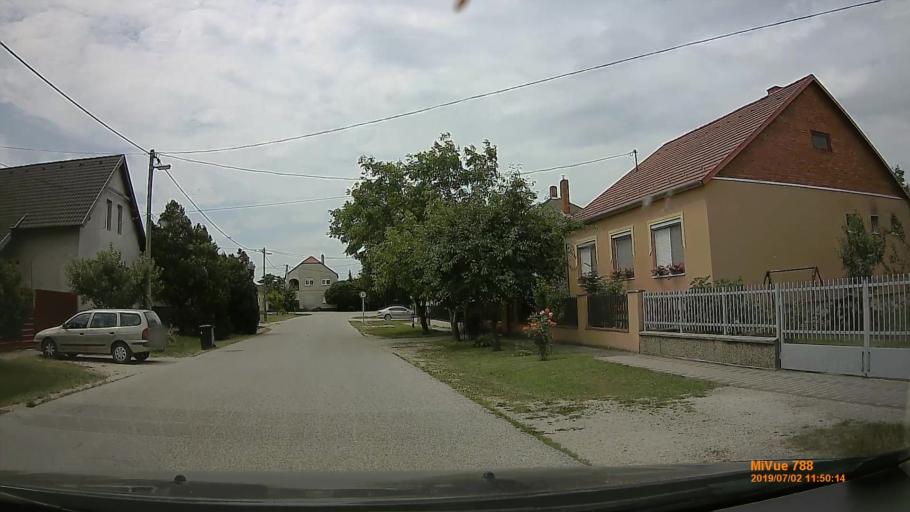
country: HU
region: Gyor-Moson-Sopron
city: Janossomorja
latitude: 47.8477
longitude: 17.1746
